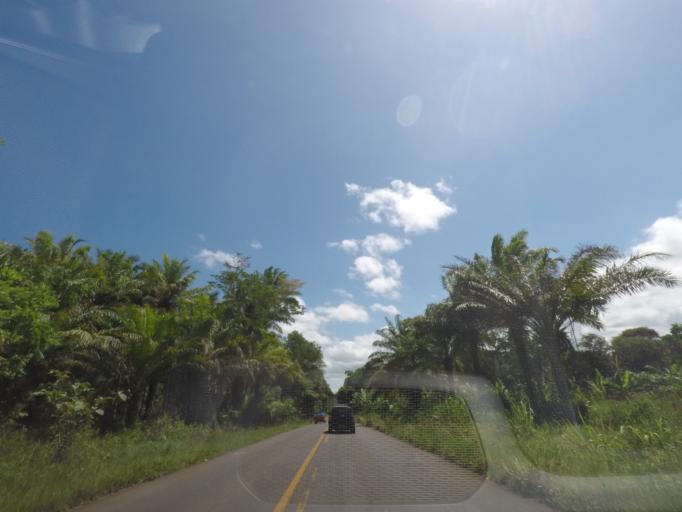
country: BR
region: Bahia
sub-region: Taperoa
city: Taperoa
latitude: -13.4742
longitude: -39.0892
